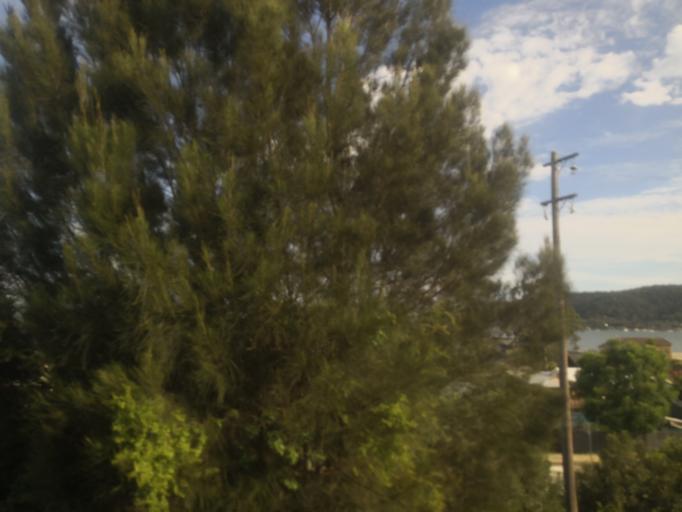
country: AU
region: New South Wales
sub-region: Gosford Shire
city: Point Clare
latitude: -33.4498
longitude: 151.3223
